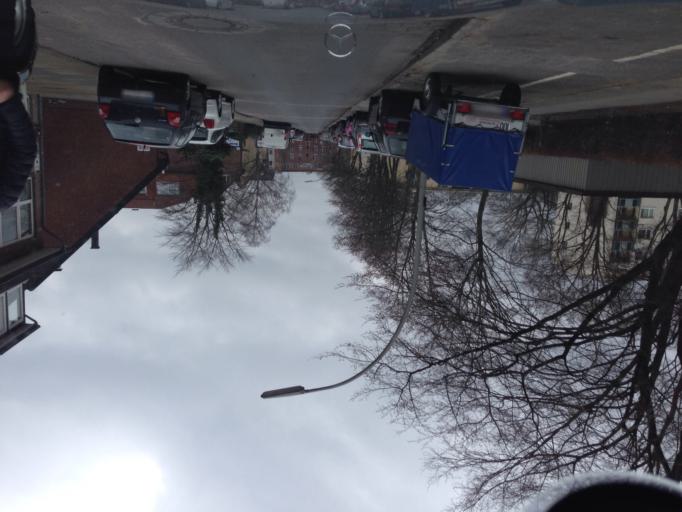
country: DE
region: Hamburg
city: Steilshoop
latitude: 53.6068
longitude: 10.0776
